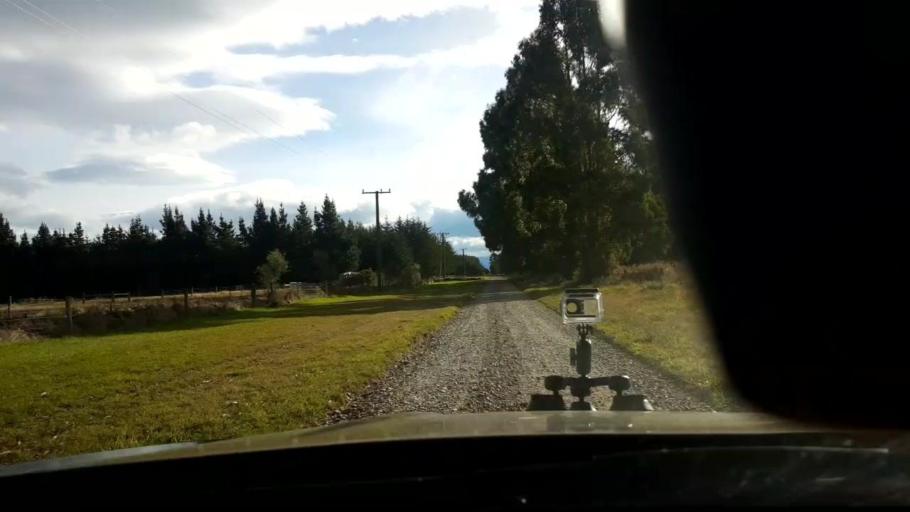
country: NZ
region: Canterbury
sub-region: Waimakariri District
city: Oxford
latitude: -43.3942
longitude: 172.2978
